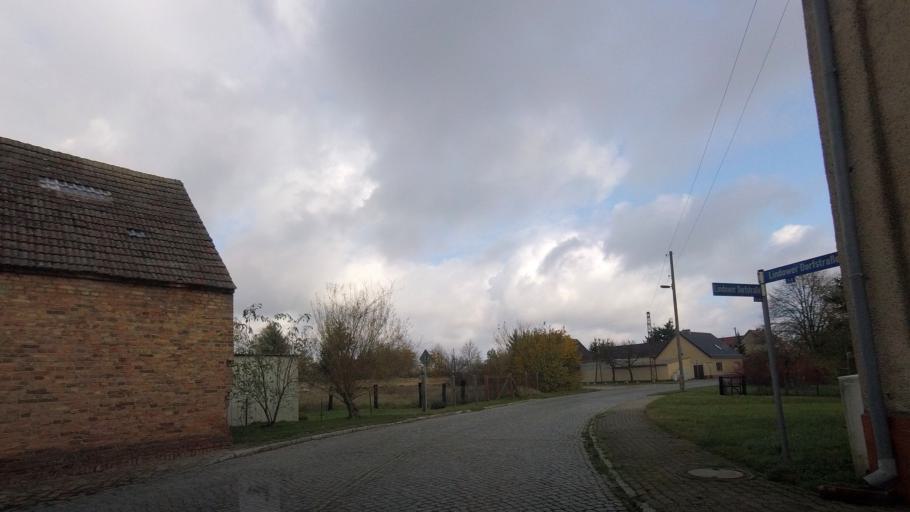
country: DE
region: Brandenburg
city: Niedergorsdorf
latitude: 52.0120
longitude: 12.9242
